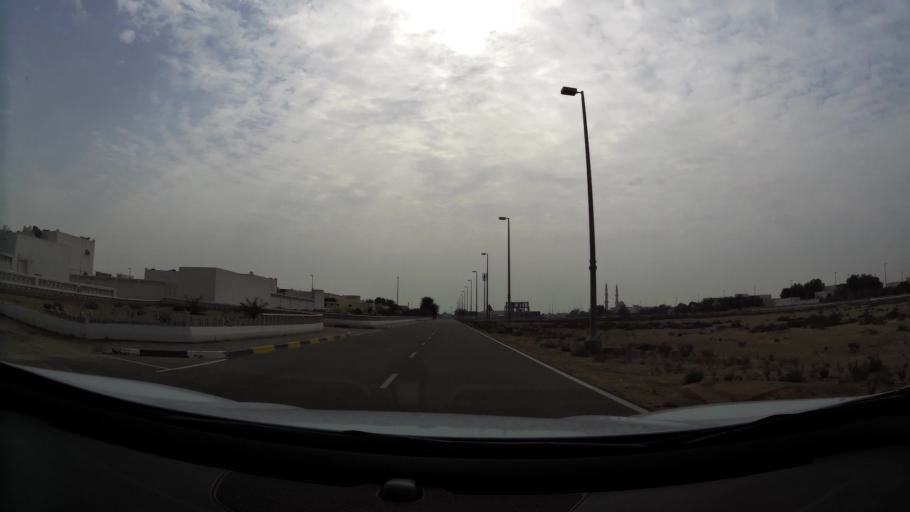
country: AE
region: Abu Dhabi
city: Abu Dhabi
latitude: 24.6779
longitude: 54.7556
